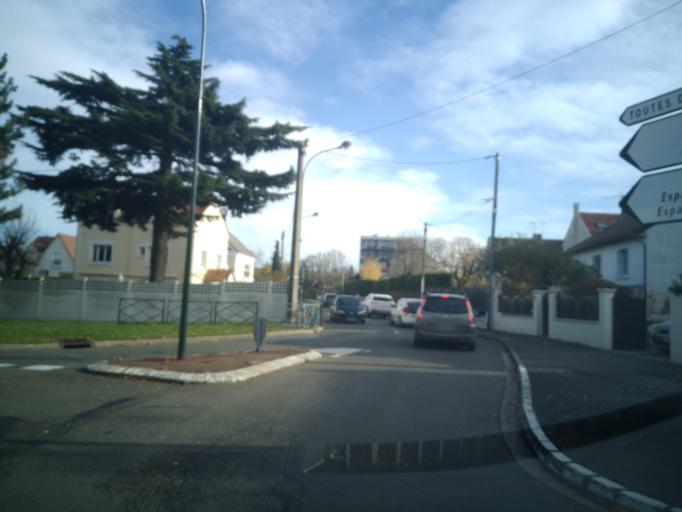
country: FR
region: Ile-de-France
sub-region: Departement des Yvelines
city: Les Clayes-sous-Bois
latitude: 48.8214
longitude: 1.9756
